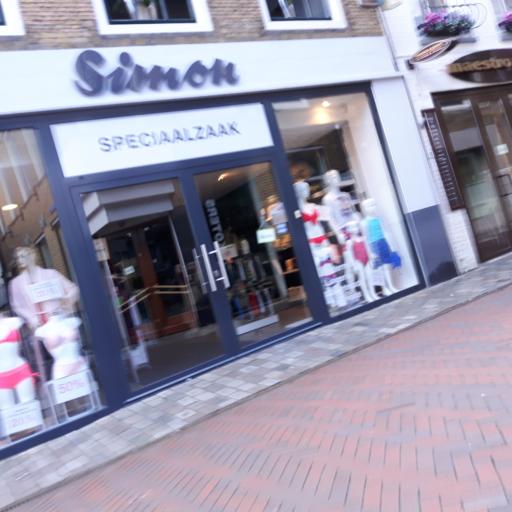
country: NL
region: Zeeland
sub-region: Gemeente Goes
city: Goes
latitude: 51.5026
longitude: 3.8917
